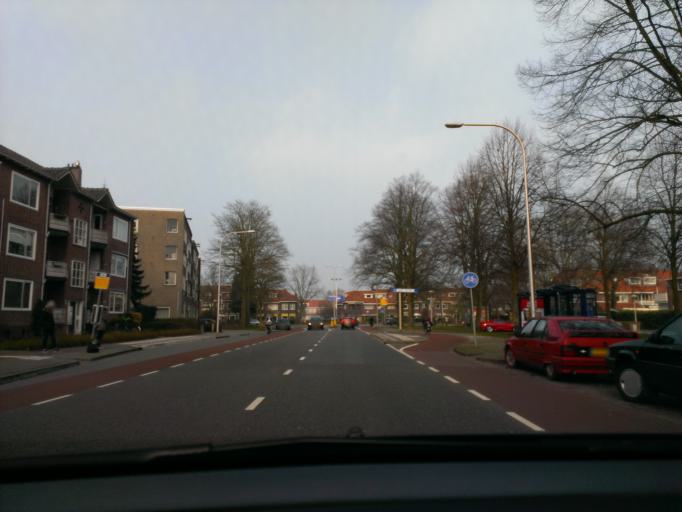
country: NL
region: Overijssel
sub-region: Gemeente Zwolle
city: Zwolle
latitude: 52.5134
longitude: 6.1088
